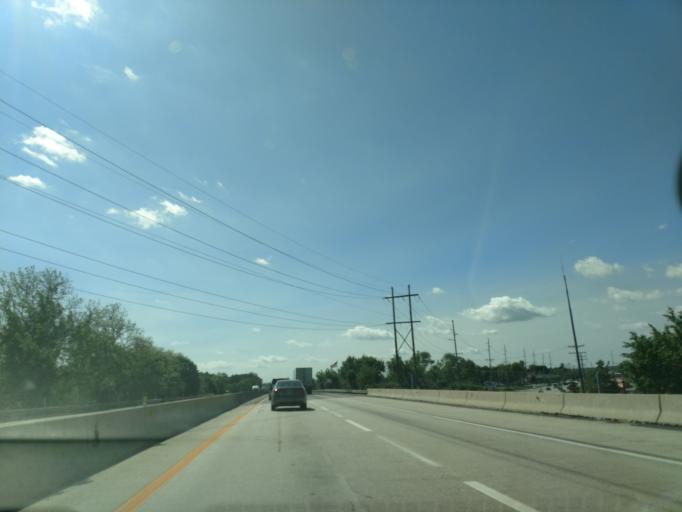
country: US
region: Pennsylvania
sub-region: Chester County
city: Chester Springs
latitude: 40.0709
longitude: -75.6800
